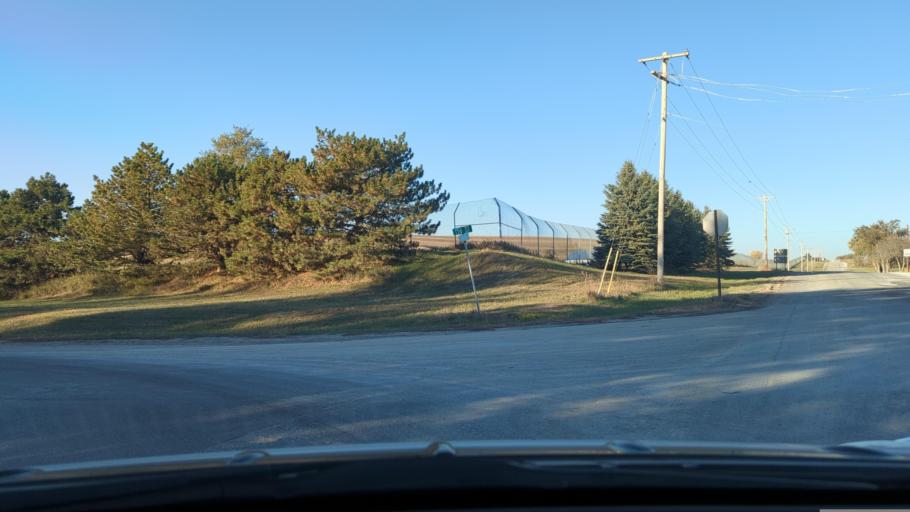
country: US
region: Nebraska
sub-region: Sarpy County
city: Springfield
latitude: 41.1035
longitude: -96.1576
